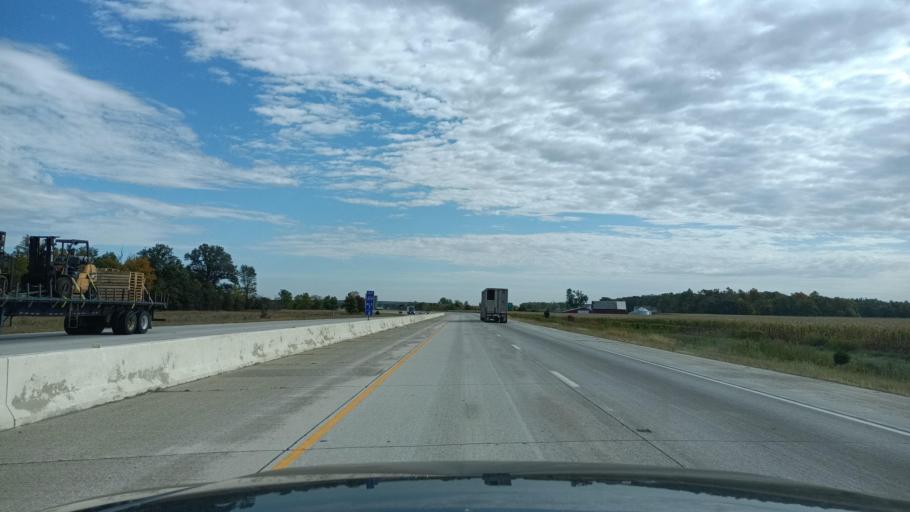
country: US
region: Indiana
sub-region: Wells County
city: Ossian
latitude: 40.9560
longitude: -85.1460
